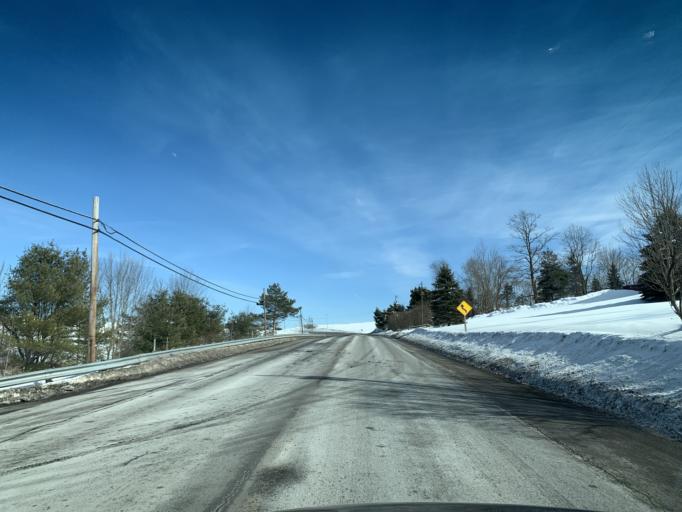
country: US
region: Maryland
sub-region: Allegany County
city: Frostburg
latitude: 39.6867
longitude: -79.0244
